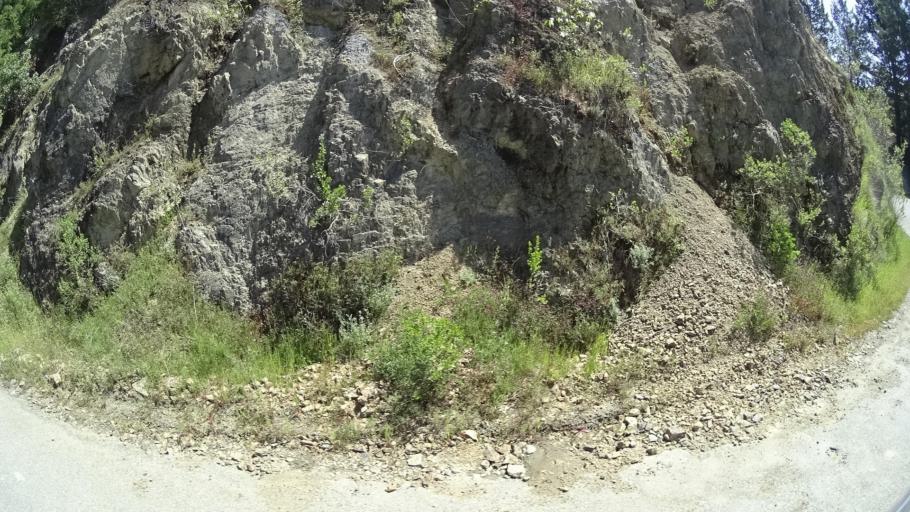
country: US
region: California
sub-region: Humboldt County
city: Redway
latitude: 40.1951
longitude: -123.5539
